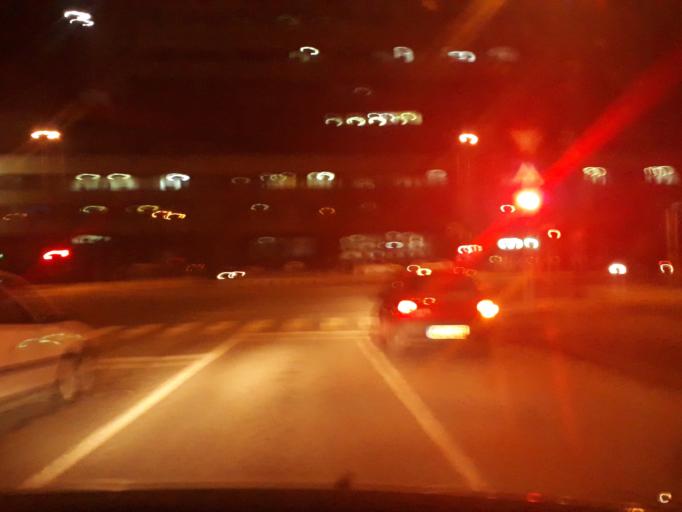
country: BA
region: Federation of Bosnia and Herzegovina
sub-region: Kanton Sarajevo
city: Sarajevo
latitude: 43.8468
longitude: 18.3540
